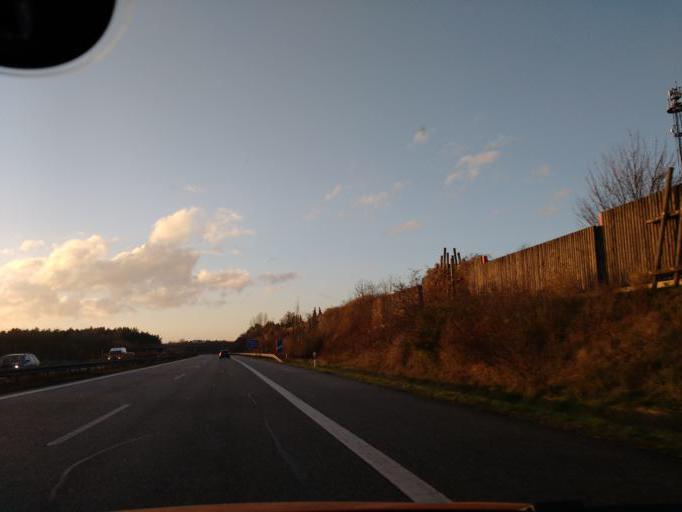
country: DE
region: Mecklenburg-Vorpommern
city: Stralendorf
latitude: 53.4851
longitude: 11.2759
